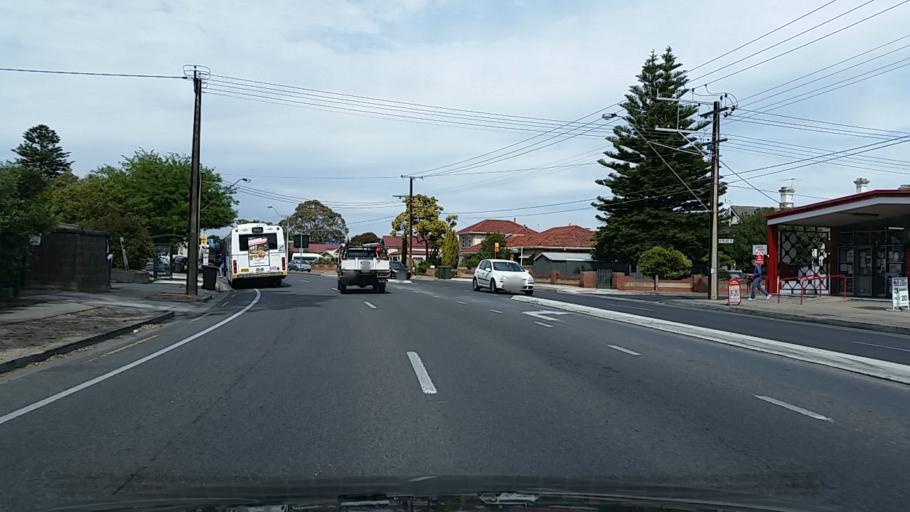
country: AU
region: South Australia
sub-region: City of West Torrens
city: Plympton
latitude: -34.9276
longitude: 138.5363
